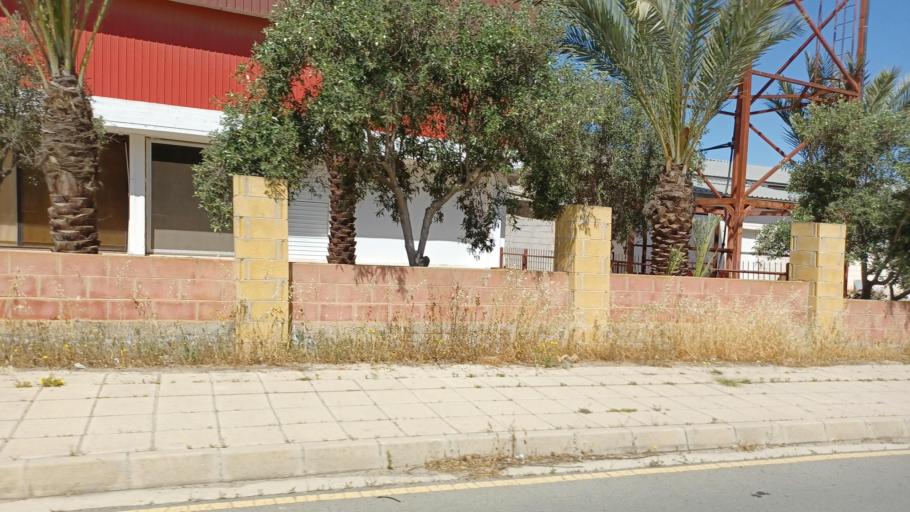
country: CY
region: Lefkosia
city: Kokkinotrimithia
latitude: 35.1518
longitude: 33.2308
